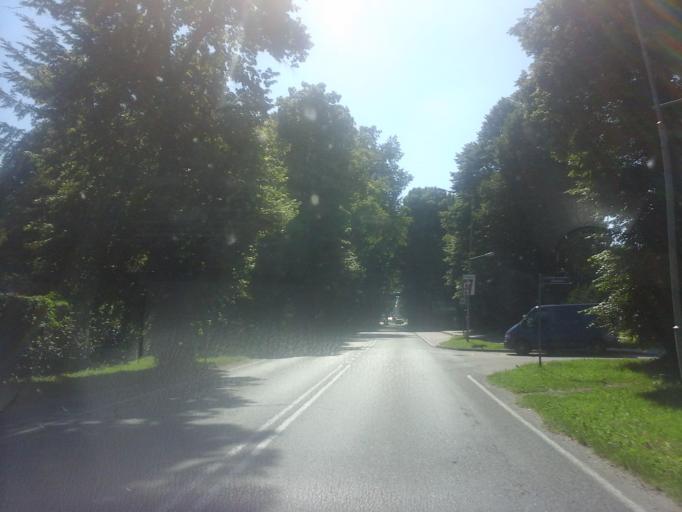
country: PL
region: West Pomeranian Voivodeship
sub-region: Powiat bialogardzki
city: Bialogard
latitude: 54.0147
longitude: 15.9560
